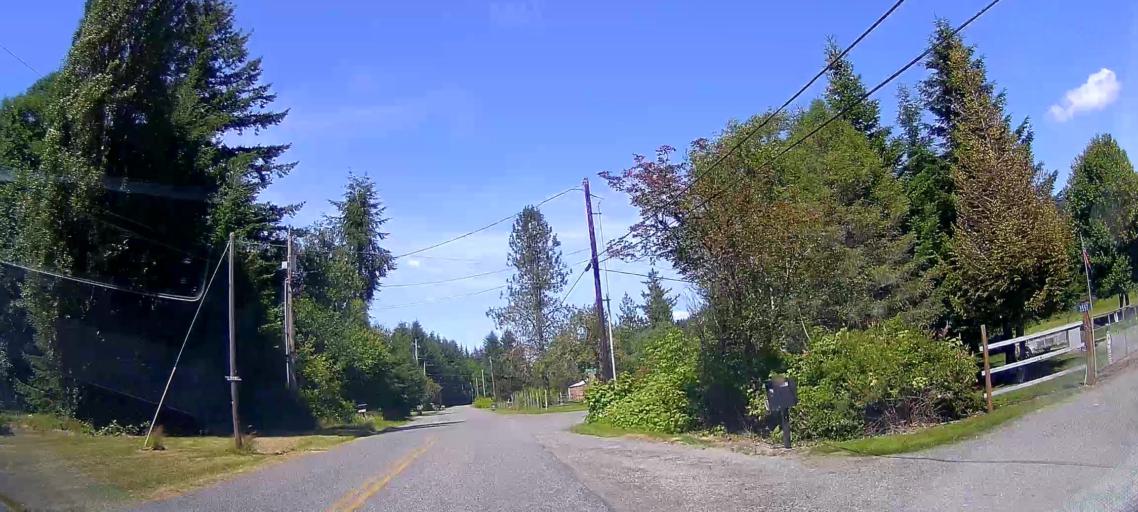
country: US
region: Washington
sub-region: Skagit County
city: Burlington
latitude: 48.5940
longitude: -122.3170
